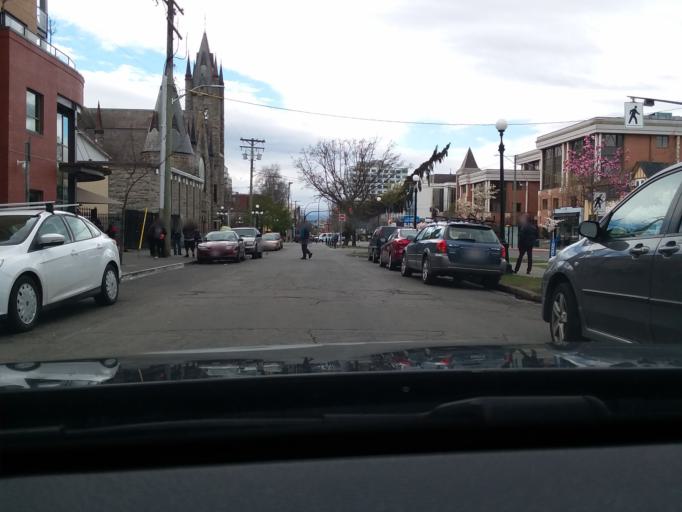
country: CA
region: British Columbia
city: Victoria
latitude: 48.4273
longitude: -123.3574
